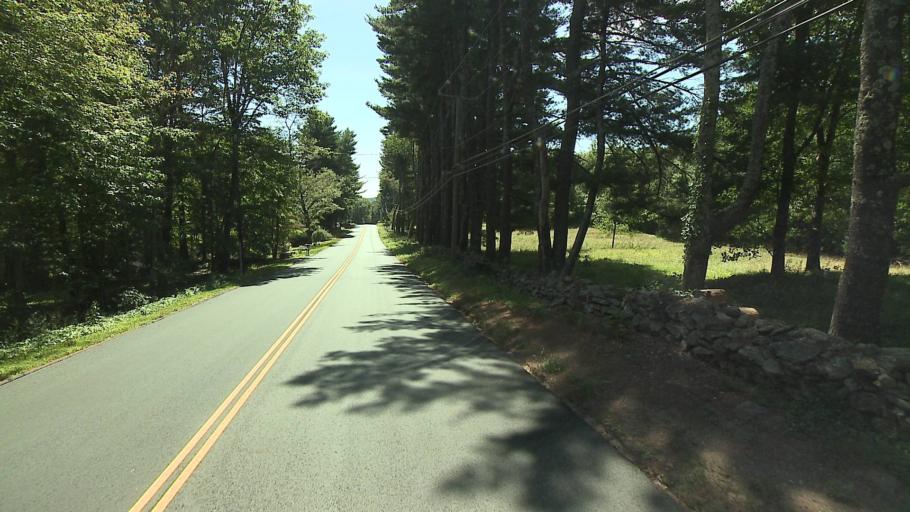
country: US
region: Connecticut
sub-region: Hartford County
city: West Simsbury
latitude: 41.9150
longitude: -72.9022
